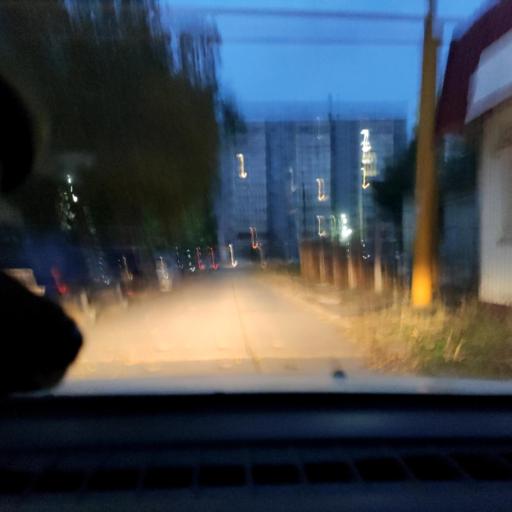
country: RU
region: Samara
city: Samara
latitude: 53.1066
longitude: 50.0831
